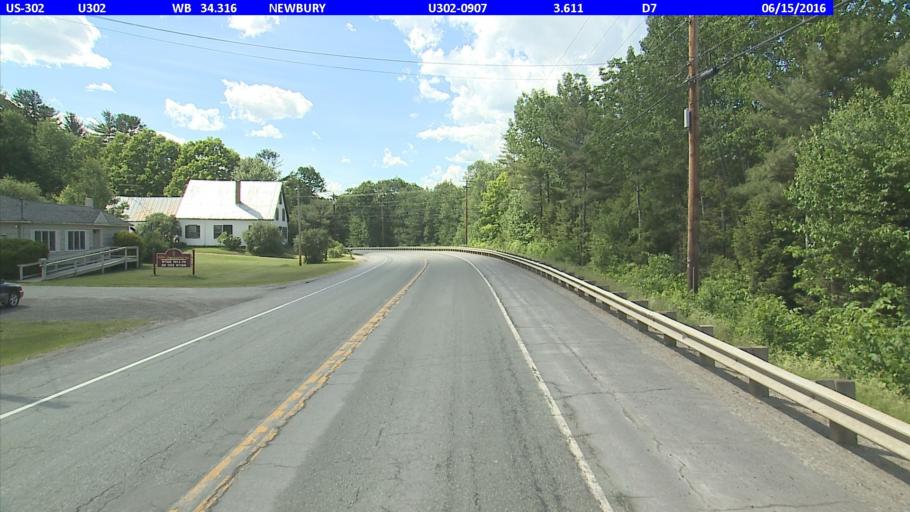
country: US
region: New Hampshire
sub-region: Grafton County
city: Woodsville
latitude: 44.1494
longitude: -72.0642
